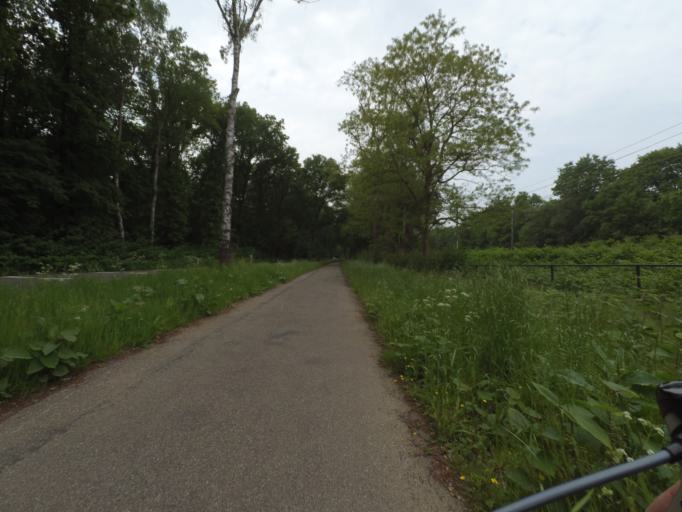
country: NL
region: Gelderland
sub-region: Gemeente Renkum
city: Wolfheze
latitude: 52.0080
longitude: 5.7785
